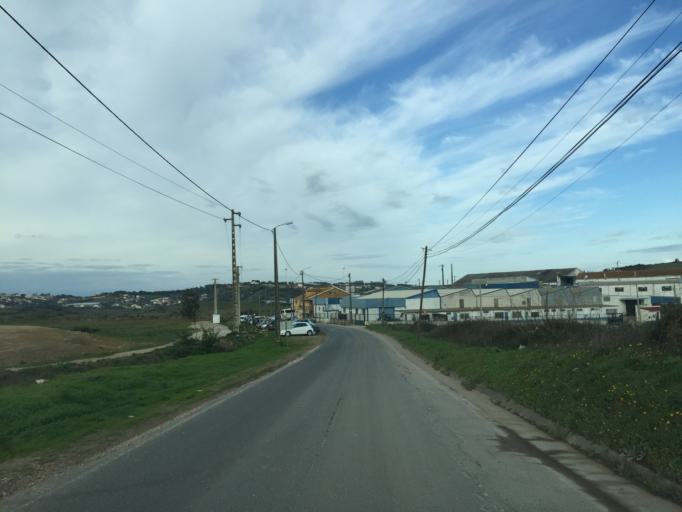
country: PT
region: Lisbon
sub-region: Odivelas
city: Canecas
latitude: 38.8254
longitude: -9.2444
